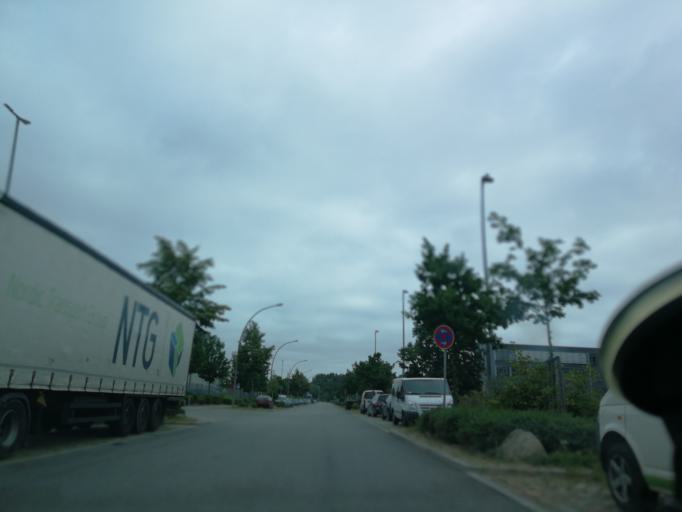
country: DE
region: Hamburg
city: Altona
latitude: 53.5056
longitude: 9.9258
